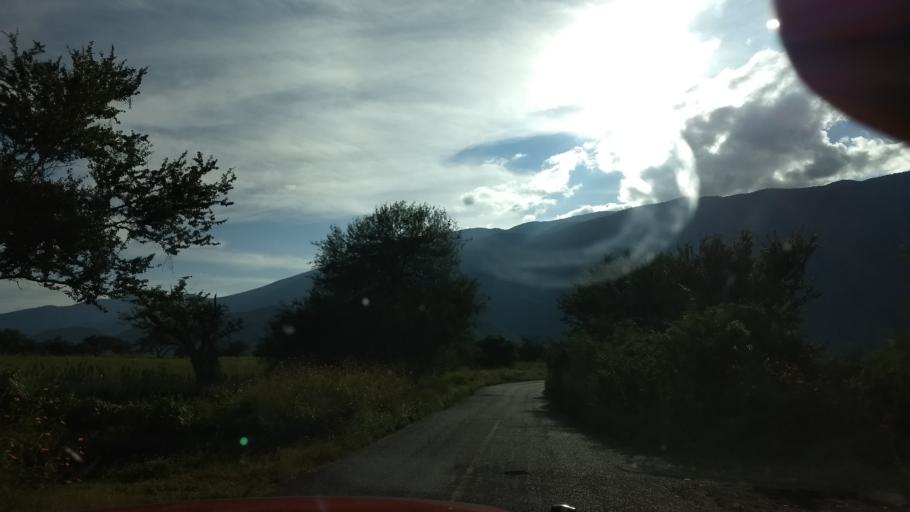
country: MX
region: Colima
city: Suchitlan
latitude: 19.4492
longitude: -103.8139
